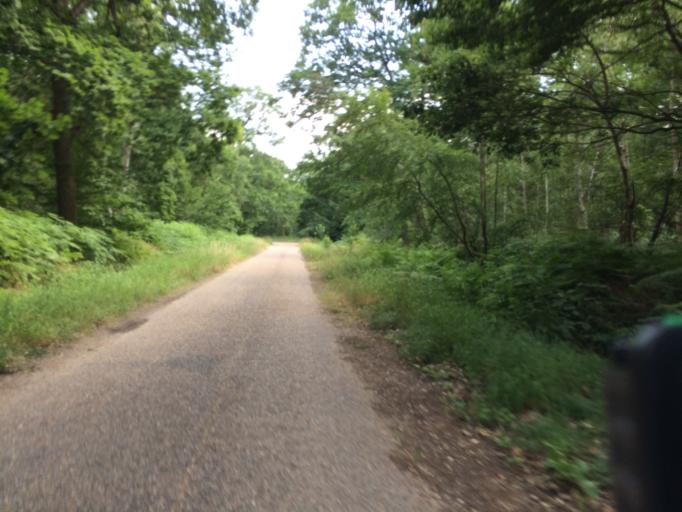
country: FR
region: Ile-de-France
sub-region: Departement de l'Essonne
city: Soisy-sur-Seine
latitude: 48.6630
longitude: 2.4452
